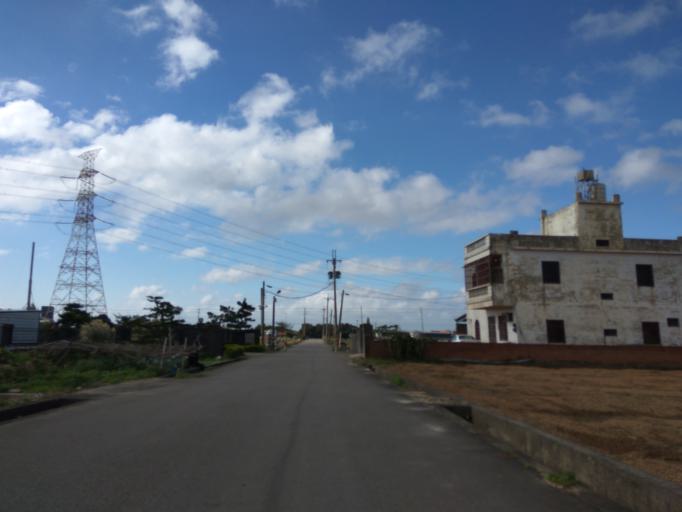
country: TW
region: Taiwan
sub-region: Hsinchu
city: Zhubei
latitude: 24.9723
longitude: 121.0772
